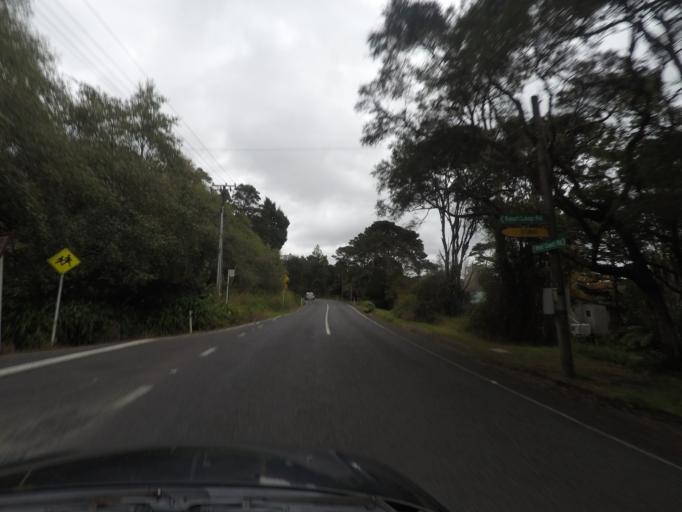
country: NZ
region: Auckland
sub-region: Auckland
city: Waitakere
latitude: -36.9224
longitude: 174.6027
